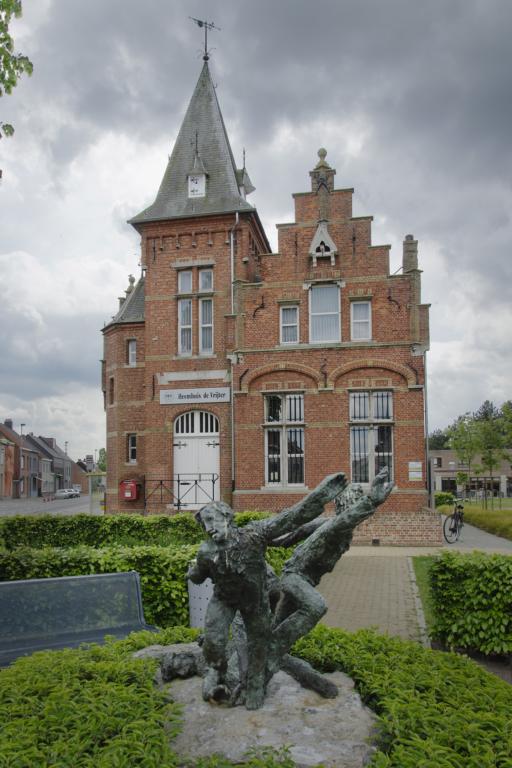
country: BE
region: Flanders
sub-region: Provincie Antwerpen
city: Lille
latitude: 51.2384
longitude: 4.8242
